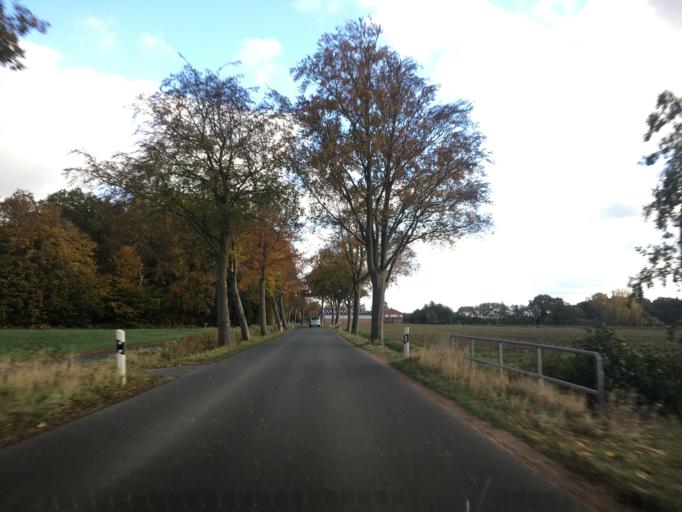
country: DE
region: North Rhine-Westphalia
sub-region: Regierungsbezirk Munster
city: Havixbeck
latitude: 51.9953
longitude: 7.4420
